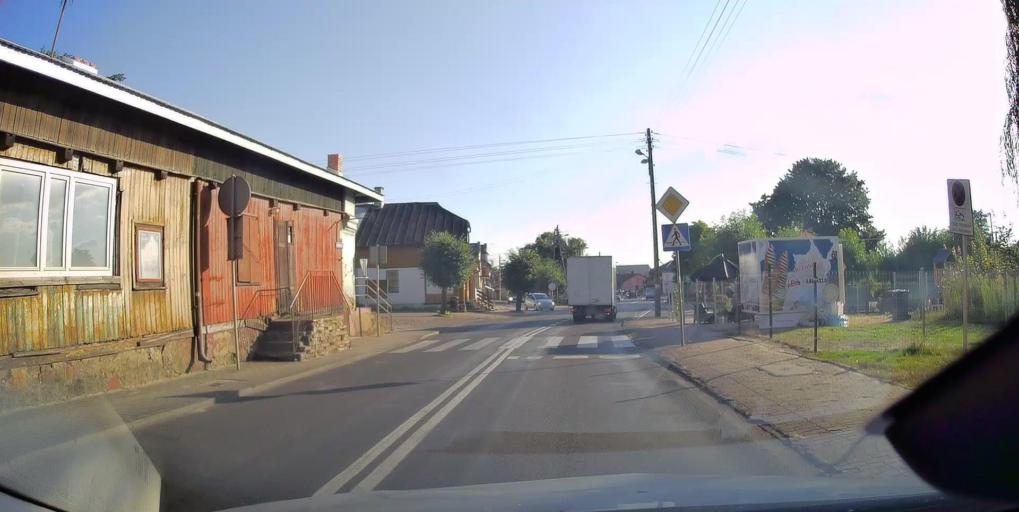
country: PL
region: Lodz Voivodeship
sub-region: Powiat rawski
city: Biala Rawska
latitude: 51.8083
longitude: 20.4734
